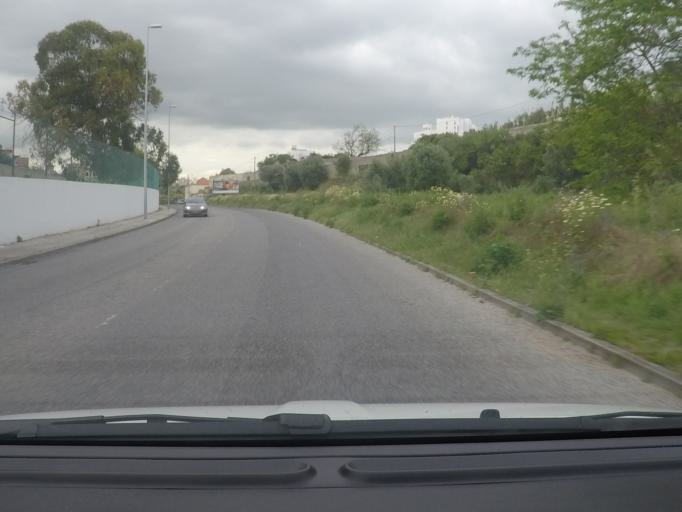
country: PT
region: Lisbon
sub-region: Lisbon
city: Lisbon
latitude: 38.7405
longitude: -9.1172
